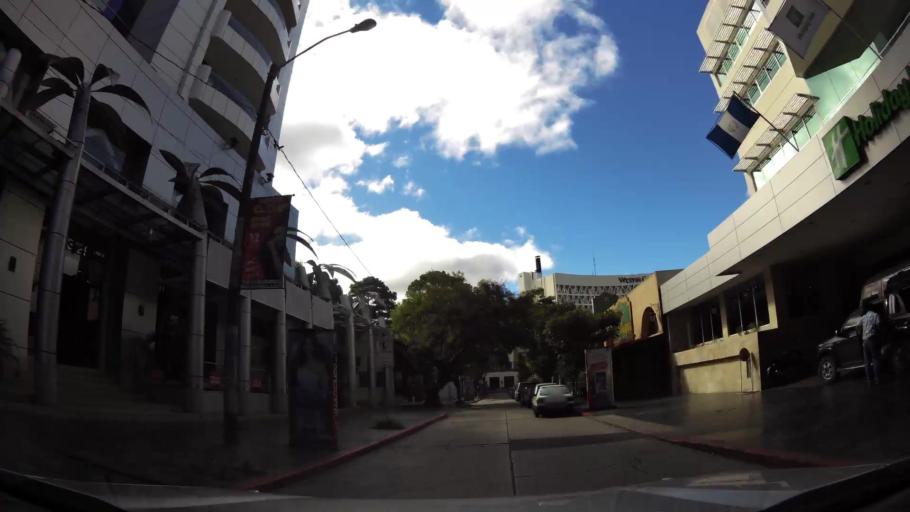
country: GT
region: Guatemala
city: Santa Catarina Pinula
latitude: 14.5992
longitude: -90.5155
